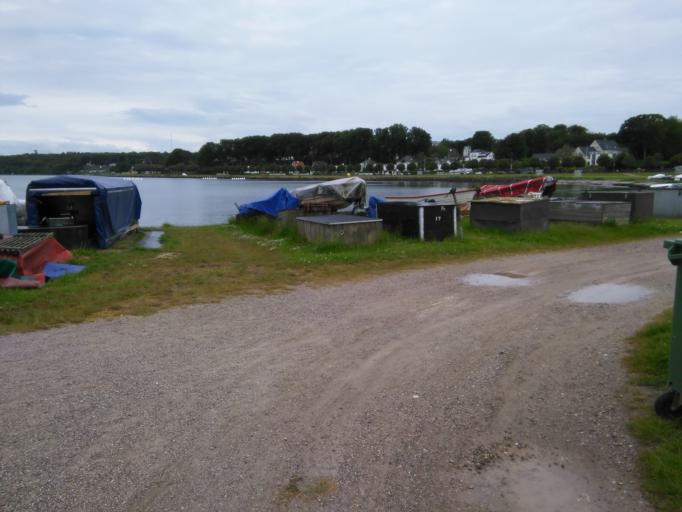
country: DK
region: Central Jutland
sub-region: Arhus Kommune
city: Arhus
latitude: 56.1376
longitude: 10.2114
